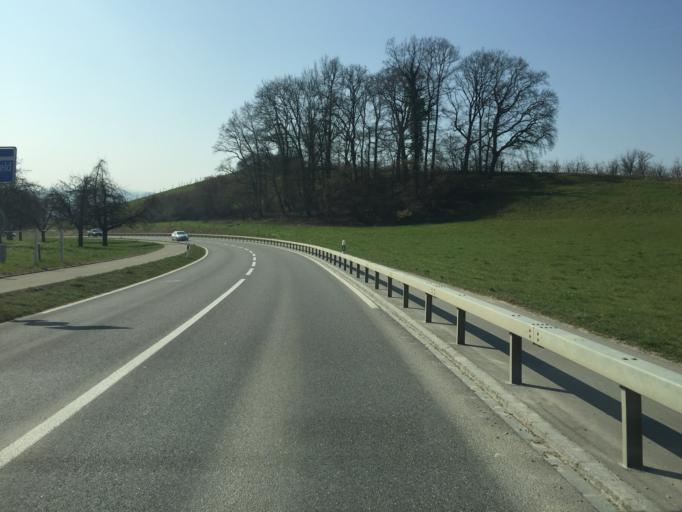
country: CH
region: Thurgau
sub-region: Frauenfeld District
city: Huttwilen
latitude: 47.5867
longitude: 8.8822
